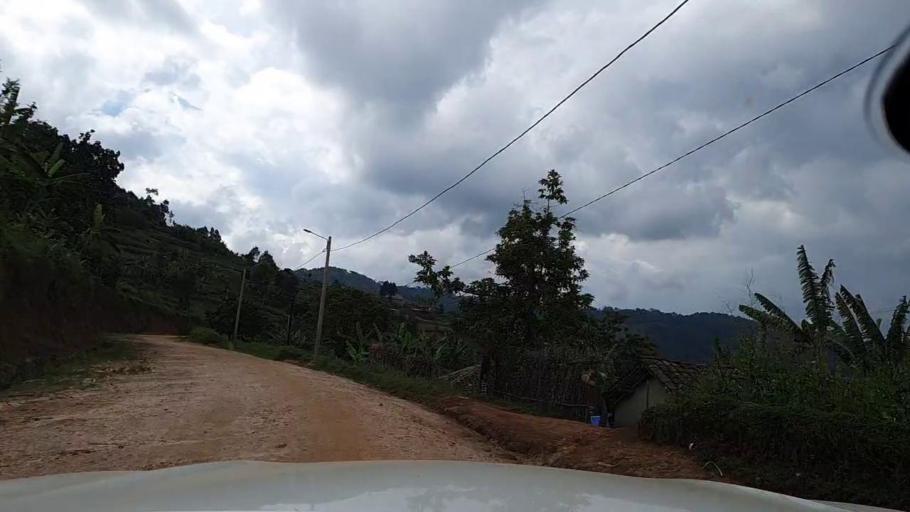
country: RW
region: Southern Province
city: Nzega
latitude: -2.7041
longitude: 29.4318
